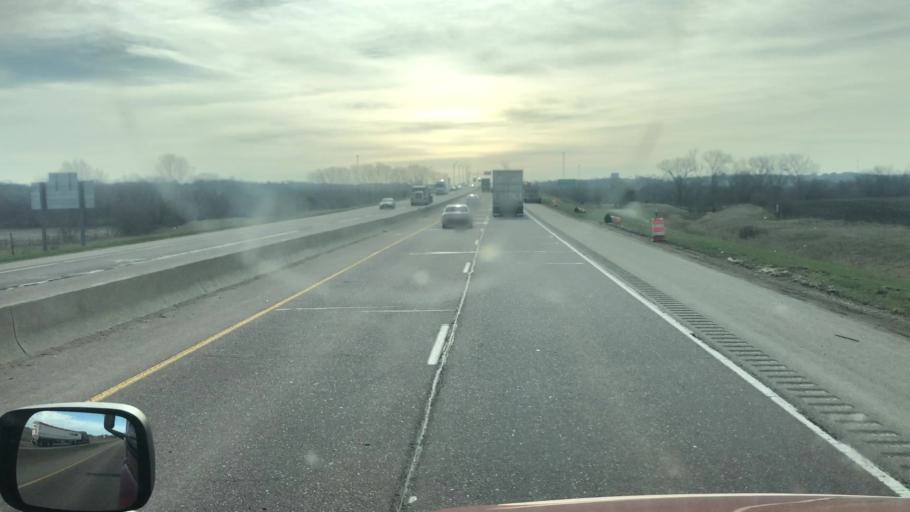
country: US
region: Nebraska
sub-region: Dakota County
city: South Sioux City
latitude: 42.4478
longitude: -96.3891
